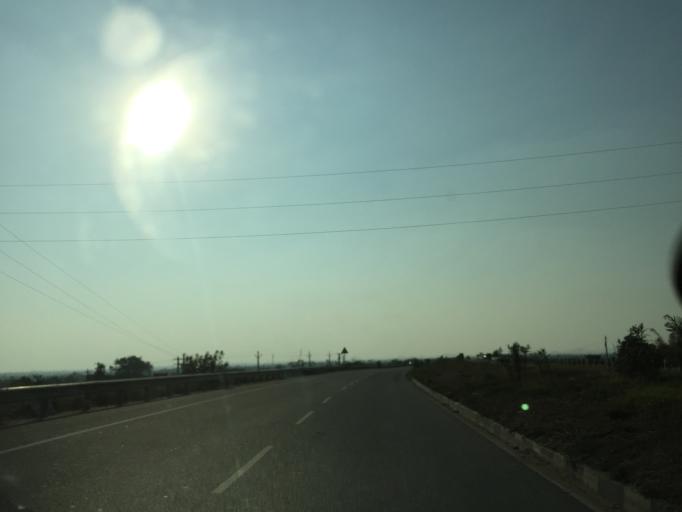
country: IN
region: Telangana
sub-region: Nalgonda
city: Gudur
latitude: 17.5030
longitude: 78.8544
